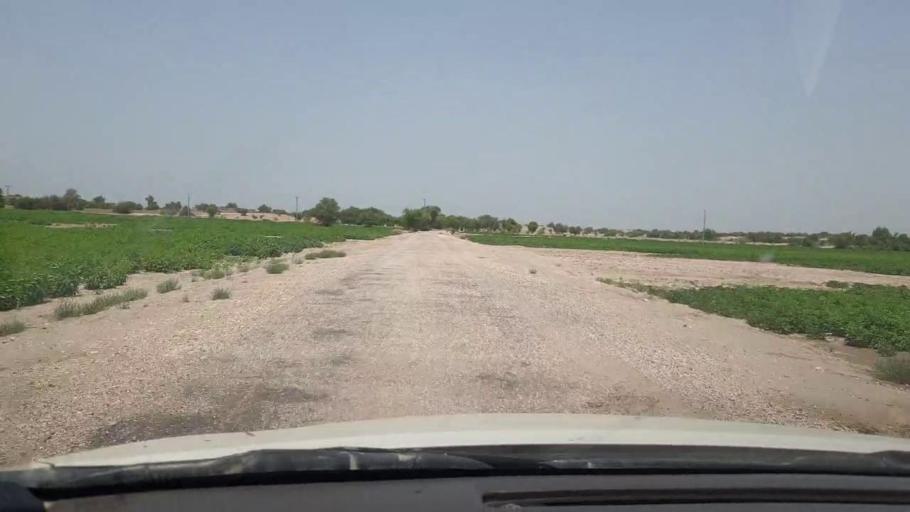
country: PK
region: Sindh
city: Rohri
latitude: 27.5130
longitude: 69.1846
